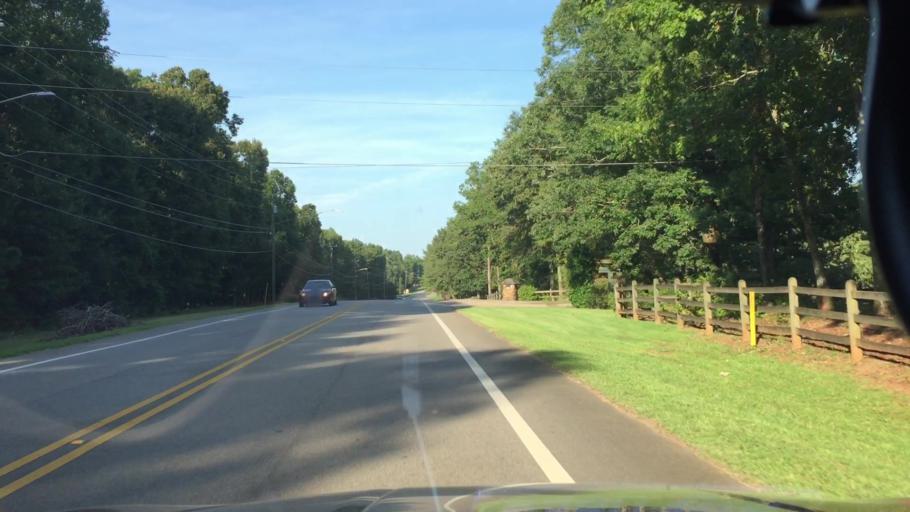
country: US
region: Alabama
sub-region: Lee County
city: Auburn
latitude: 32.5954
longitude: -85.4255
